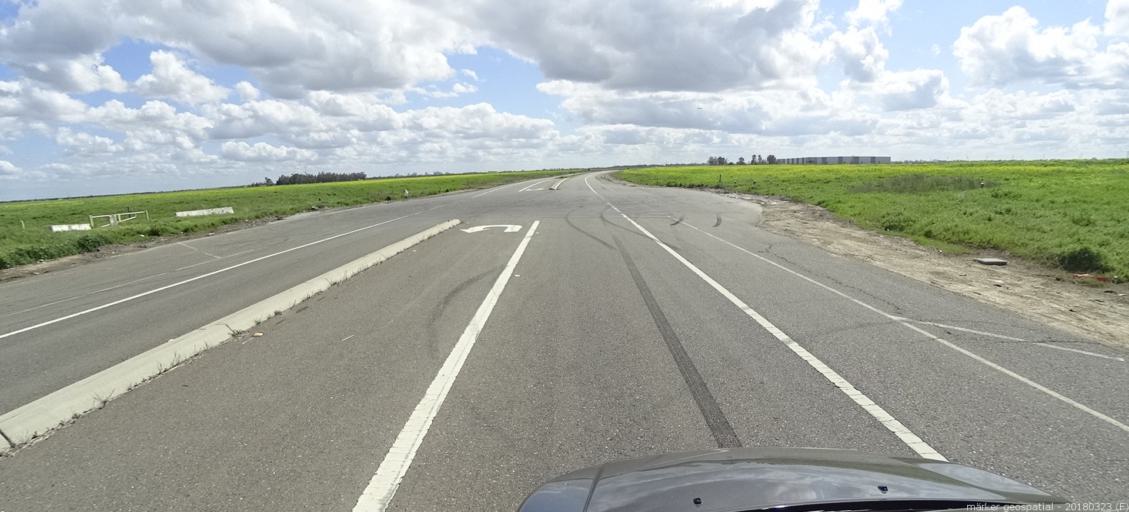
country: US
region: California
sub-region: Sacramento County
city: Elverta
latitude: 38.6956
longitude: -121.5702
